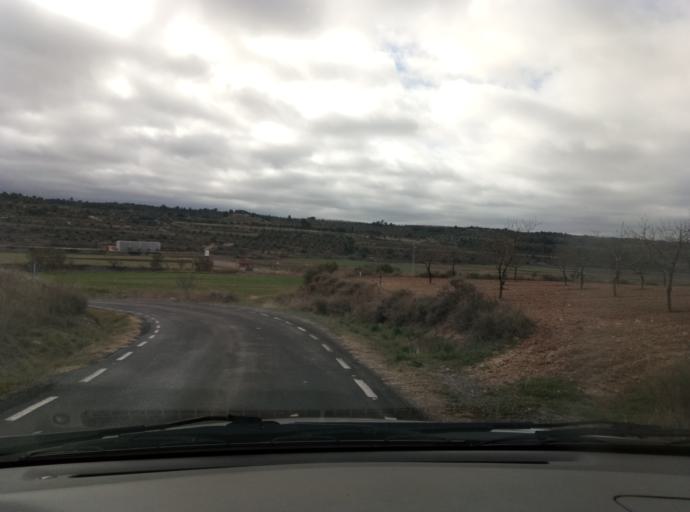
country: ES
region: Catalonia
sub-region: Provincia de Lleida
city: Vallbona de les Monges
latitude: 41.5604
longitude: 1.0643
